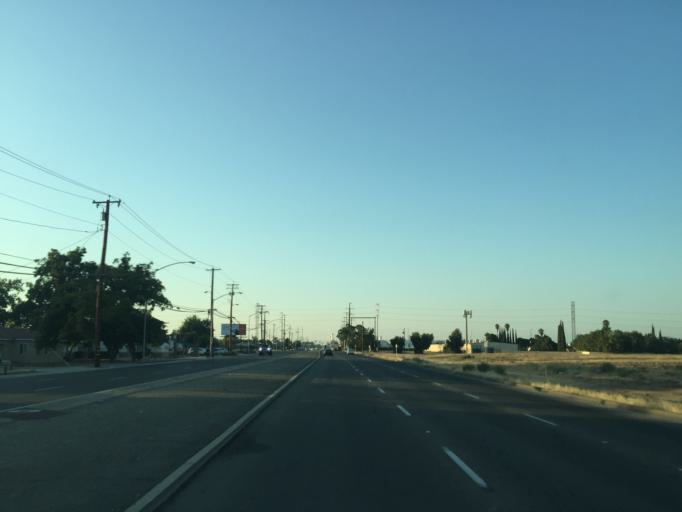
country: US
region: California
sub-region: Fresno County
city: Sunnyside
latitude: 36.7458
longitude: -119.7000
